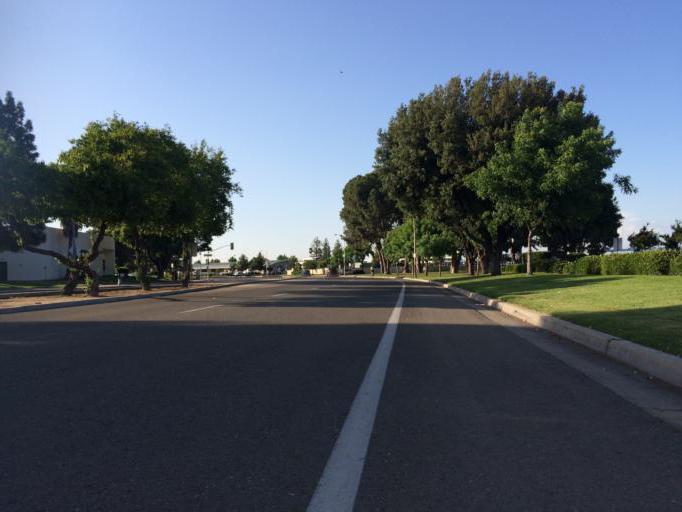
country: US
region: California
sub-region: Fresno County
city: Sunnyside
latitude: 36.7692
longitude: -119.7222
